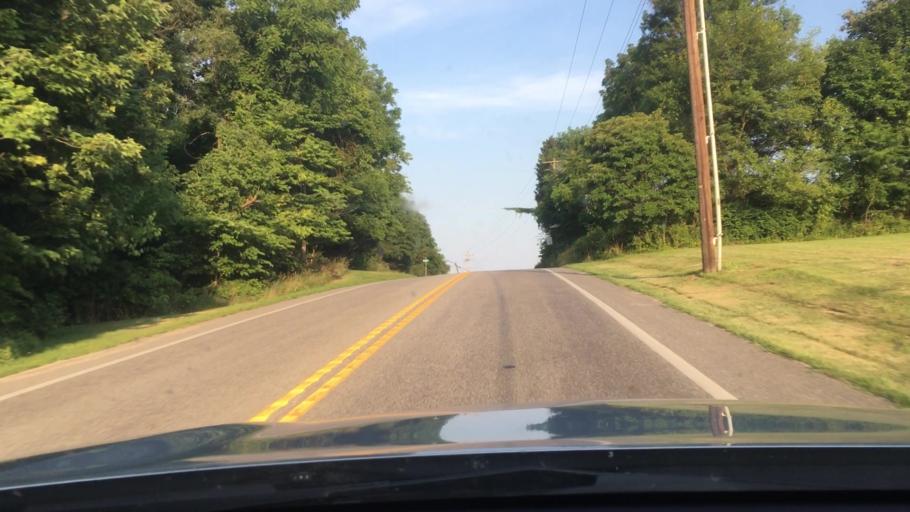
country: US
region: Pennsylvania
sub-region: Cumberland County
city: Boiling Springs
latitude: 40.1722
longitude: -77.1197
